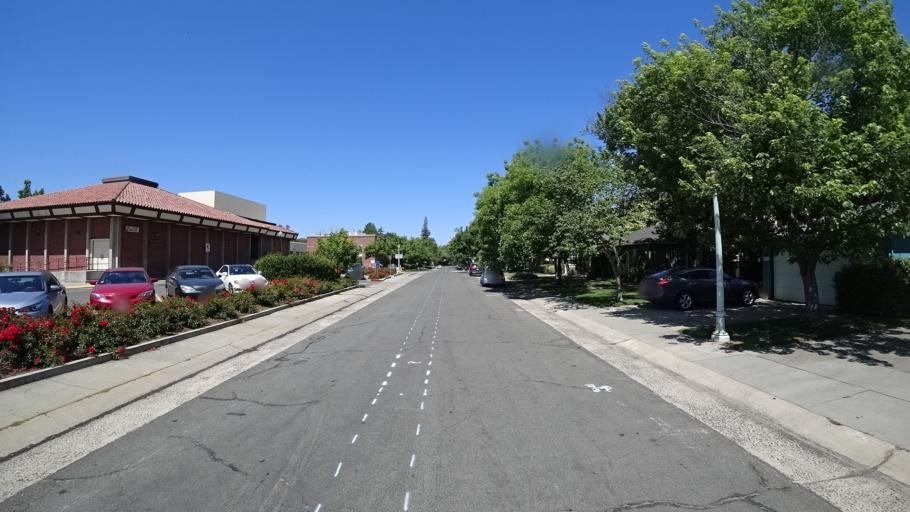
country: US
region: California
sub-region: Sacramento County
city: Sacramento
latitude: 38.5425
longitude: -121.4891
